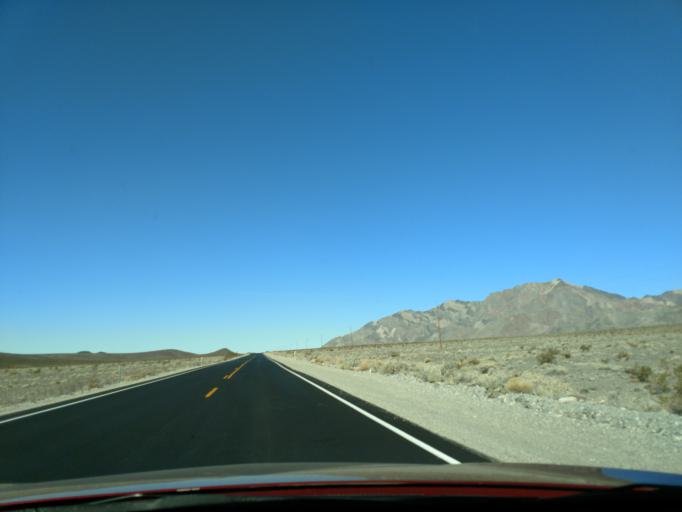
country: US
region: Nevada
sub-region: Nye County
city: Pahrump
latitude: 36.3261
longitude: -116.5653
